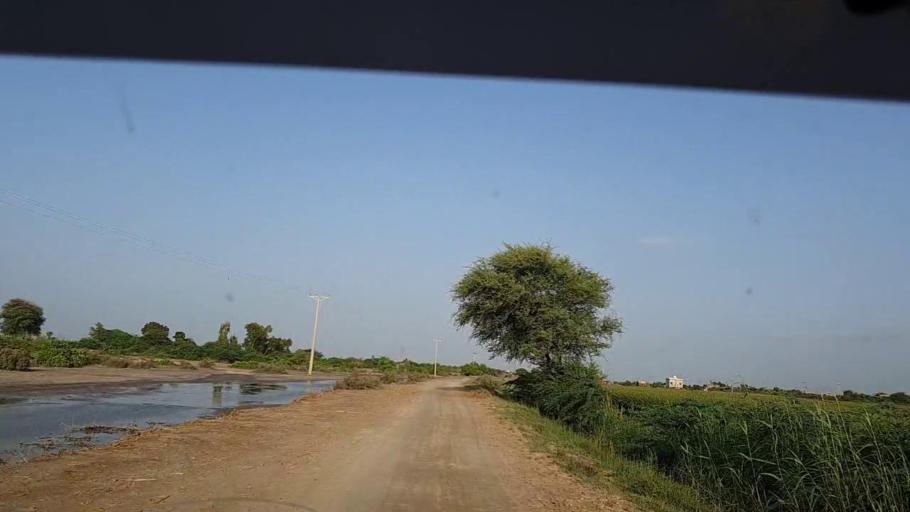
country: PK
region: Sindh
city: Badin
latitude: 24.5523
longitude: 68.8662
